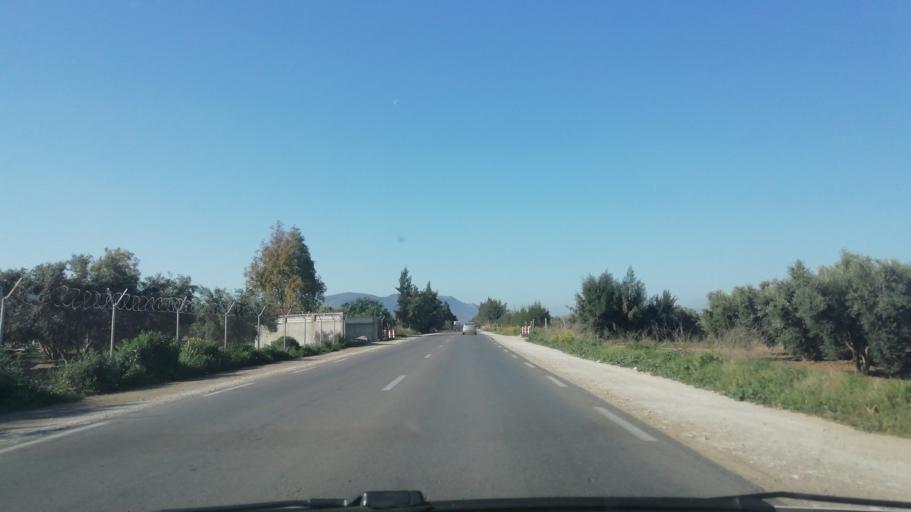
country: DZ
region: Mascara
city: Sig
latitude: 35.5502
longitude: -0.1139
